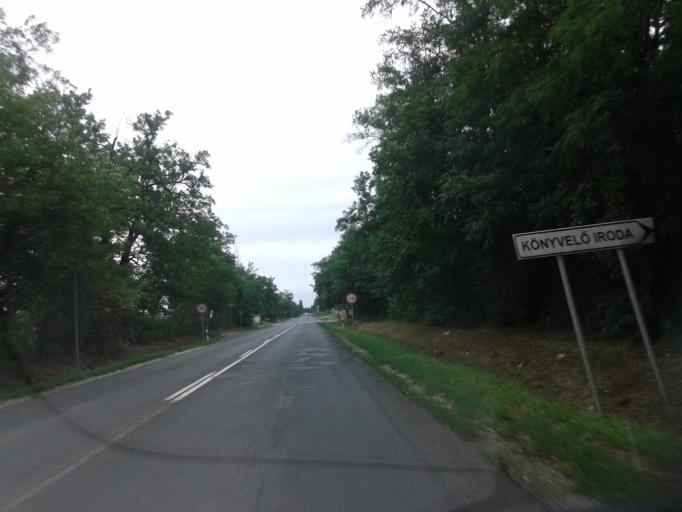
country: HU
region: Pest
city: Kiskunlachaza
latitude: 47.2357
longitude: 19.0208
